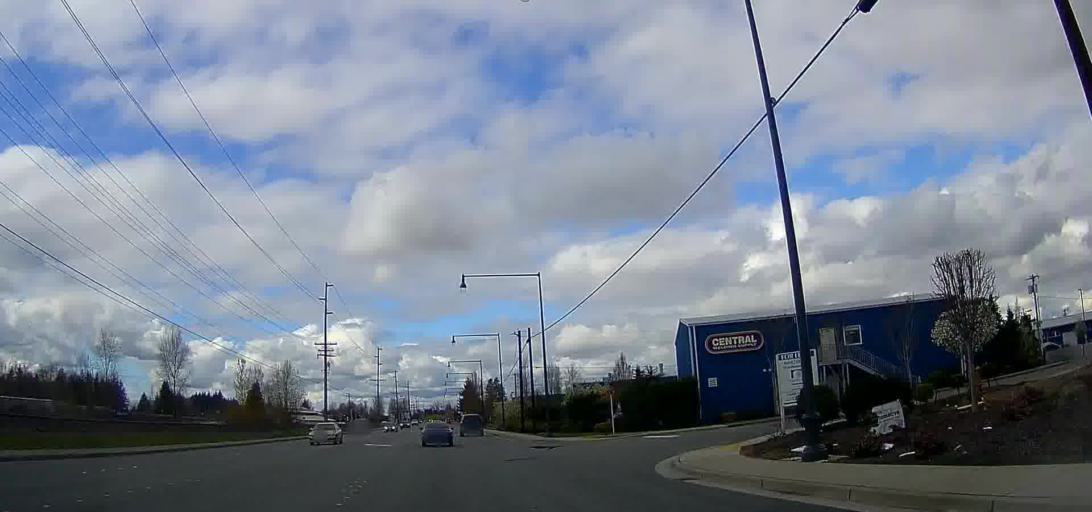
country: US
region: Washington
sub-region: Snohomish County
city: Smokey Point
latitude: 48.1155
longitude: -122.1809
